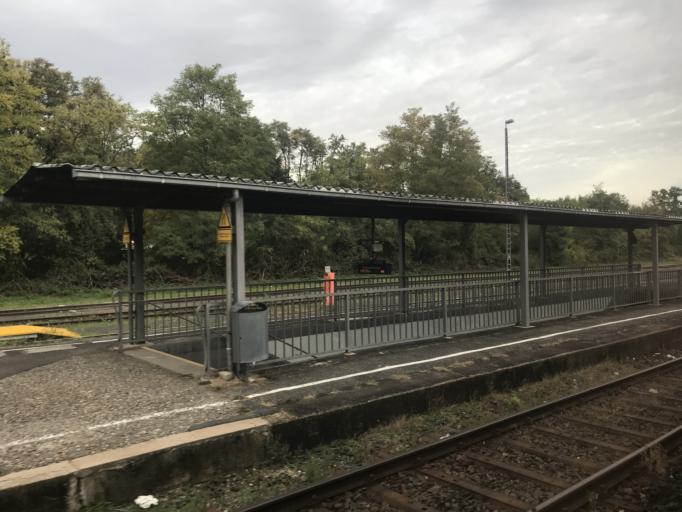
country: DE
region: Rheinland-Pfalz
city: Alzey
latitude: 49.7505
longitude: 8.1098
